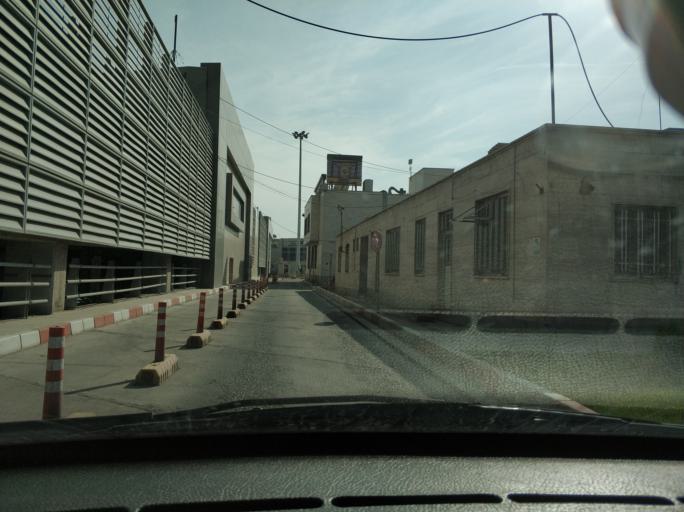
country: IR
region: Tehran
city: Tehran
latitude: 35.6936
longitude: 51.3222
